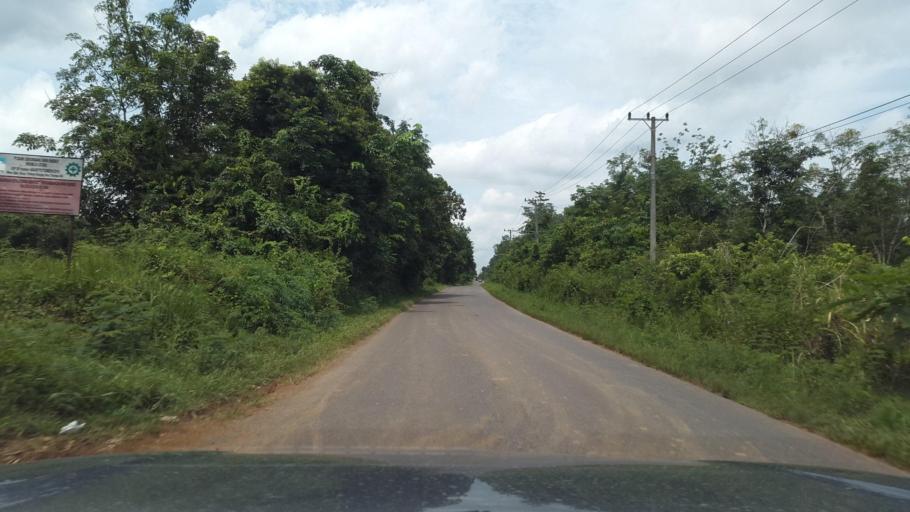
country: ID
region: South Sumatra
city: Gunungmegang Dalam
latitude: -3.3538
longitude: 103.9252
